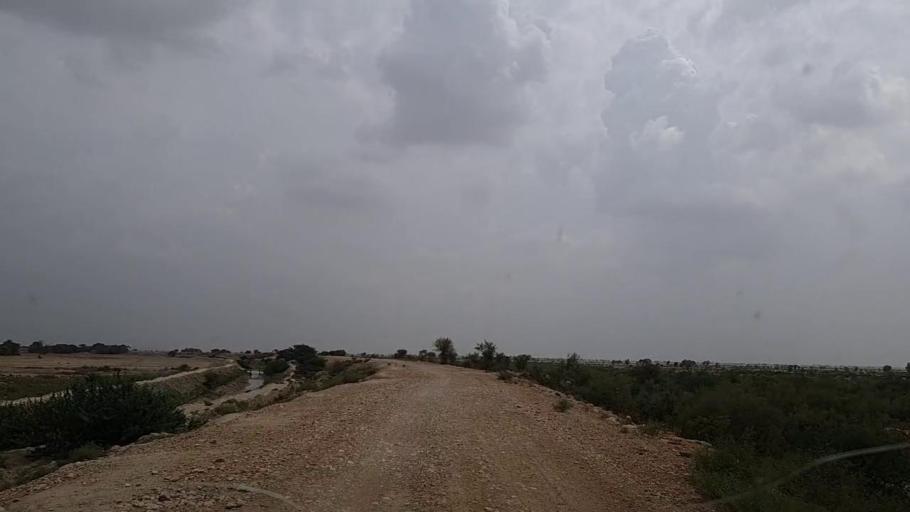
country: PK
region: Sindh
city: Johi
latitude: 26.7293
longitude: 67.5784
